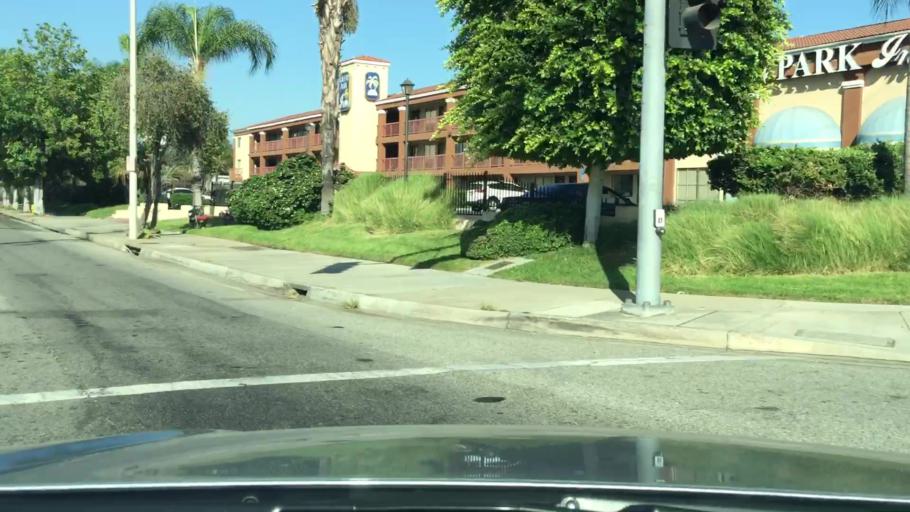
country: US
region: California
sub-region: Los Angeles County
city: West Puente Valley
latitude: 34.0672
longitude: -117.9731
